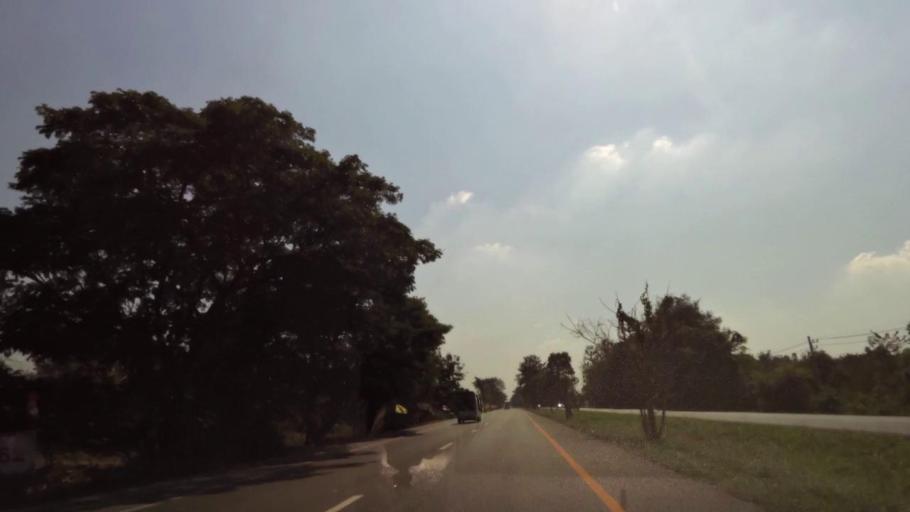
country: TH
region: Phichit
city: Bueng Na Rang
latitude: 16.2353
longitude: 100.1255
